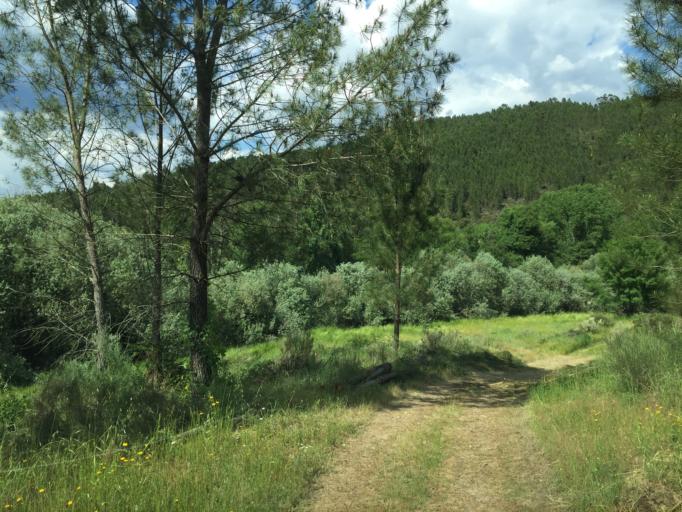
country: PT
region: Coimbra
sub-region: Pampilhosa da Serra
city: Pampilhosa da Serra
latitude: 40.0479
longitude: -7.8039
